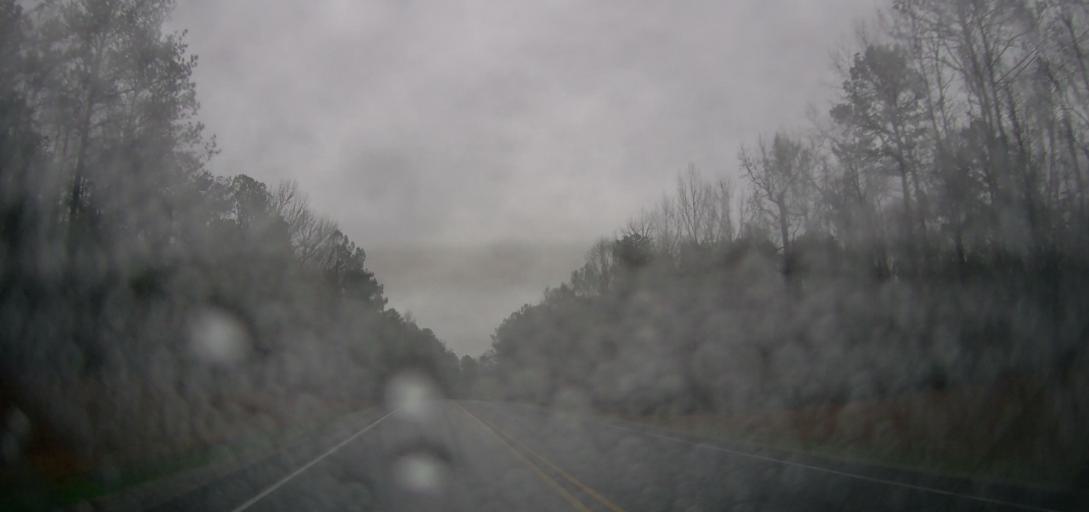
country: US
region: Alabama
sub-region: Chilton County
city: Clanton
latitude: 32.6121
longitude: -86.7207
